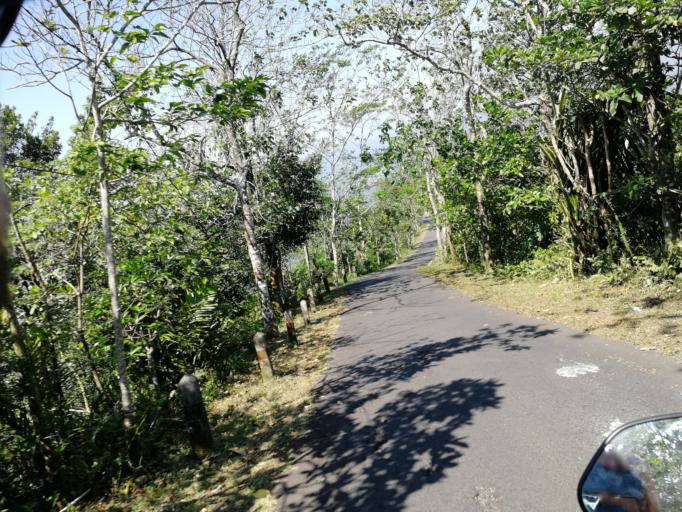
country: ID
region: Bali
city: Tiyingtali Kelod
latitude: -8.3913
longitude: 115.6376
